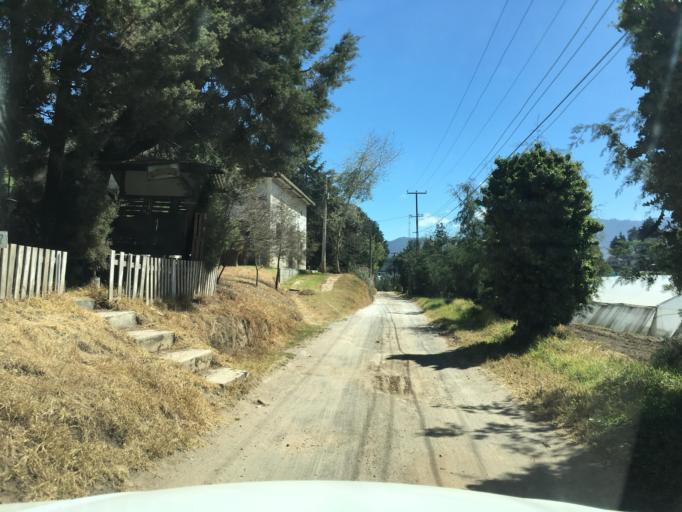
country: GT
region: Quetzaltenango
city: Quetzaltenango
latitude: 14.8445
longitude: -91.4933
